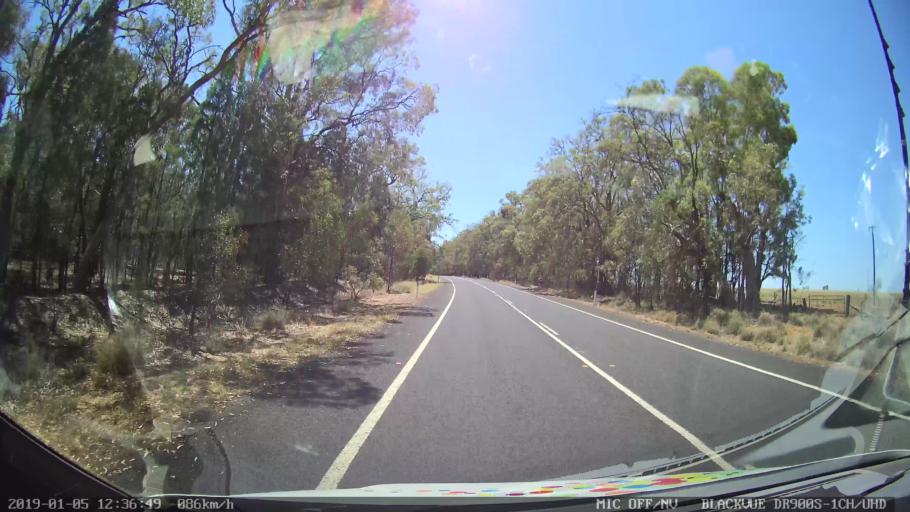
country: AU
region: New South Wales
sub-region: Warrumbungle Shire
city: Coonabarabran
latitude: -31.2062
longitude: 149.4461
